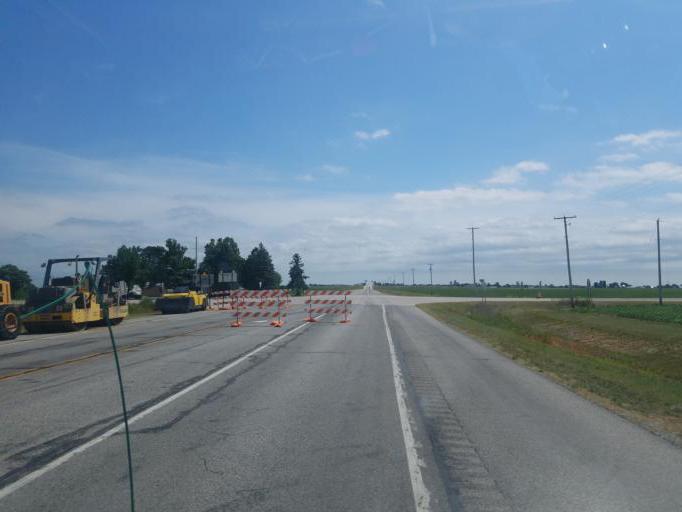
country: US
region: Indiana
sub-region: Allen County
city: Woodburn
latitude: 41.1550
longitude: -84.8488
